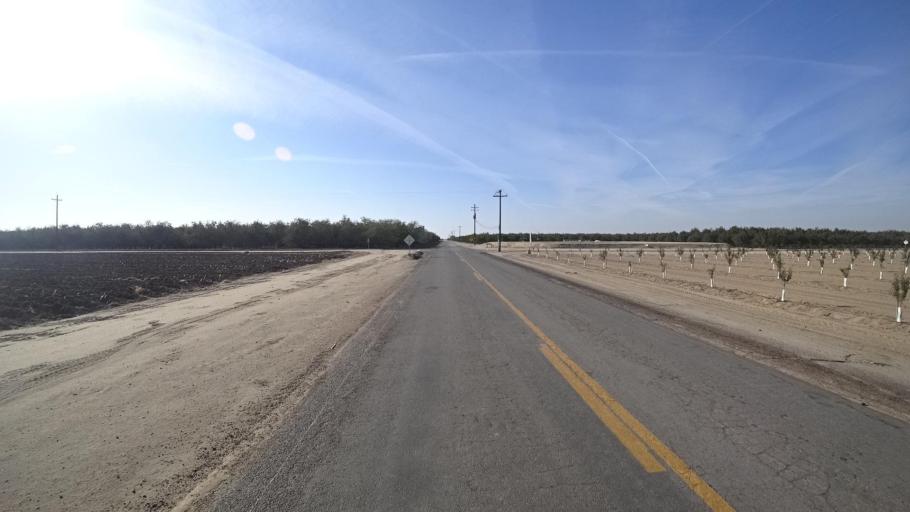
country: US
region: California
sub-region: Kern County
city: McFarland
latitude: 35.7032
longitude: -119.2935
